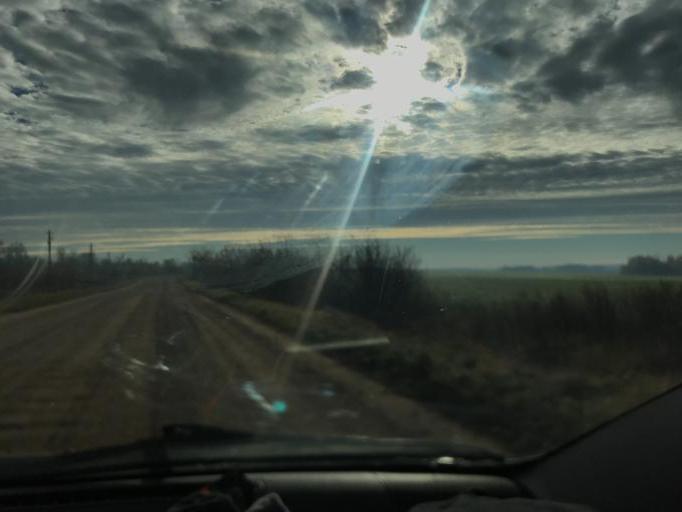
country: BY
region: Vitebsk
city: Haradok
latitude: 55.4556
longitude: 30.0133
